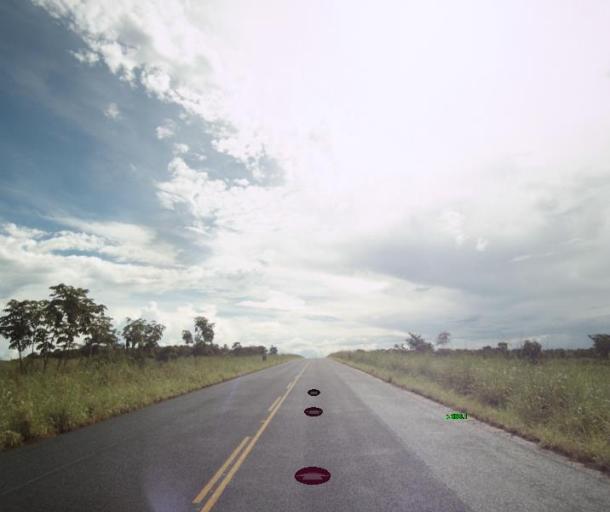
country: BR
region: Goias
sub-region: Sao Miguel Do Araguaia
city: Sao Miguel do Araguaia
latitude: -13.2974
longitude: -50.3377
